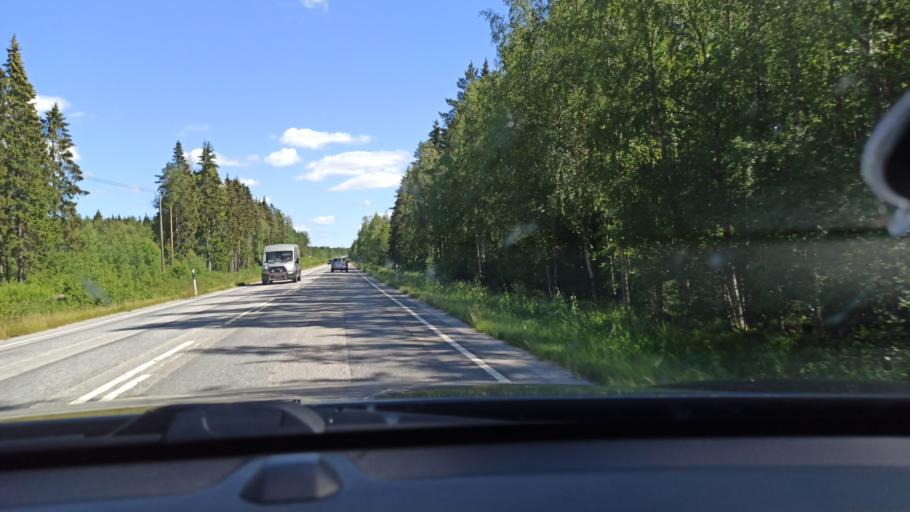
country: FI
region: Ostrobothnia
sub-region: Vaasa
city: Malax
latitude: 62.9645
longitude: 21.5795
